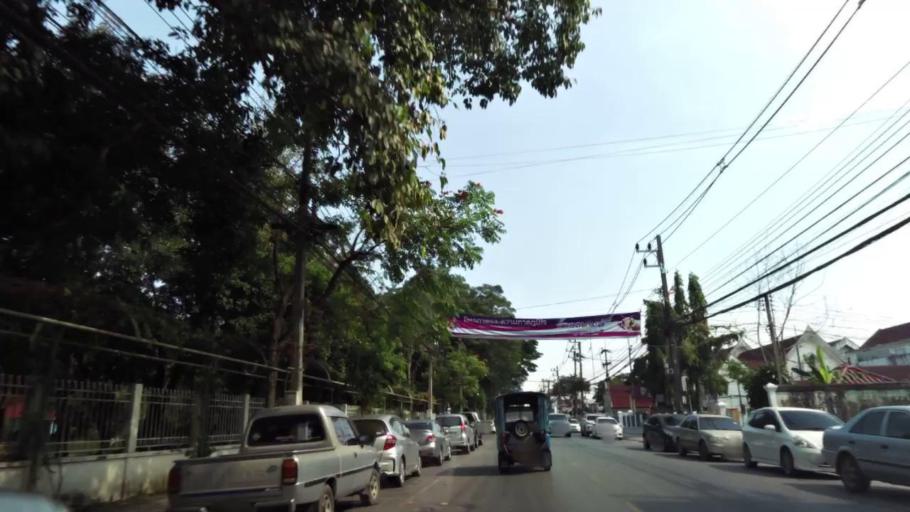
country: TH
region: Chiang Rai
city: Chiang Rai
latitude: 19.9088
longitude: 99.8314
